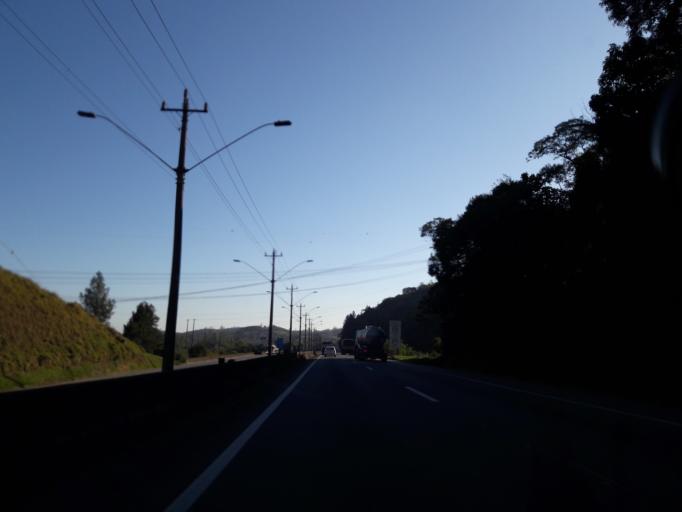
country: BR
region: Sao Paulo
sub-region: Sao Lourenco Da Serra
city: Sao Lourenco da Serra
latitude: -23.8869
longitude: -46.9777
